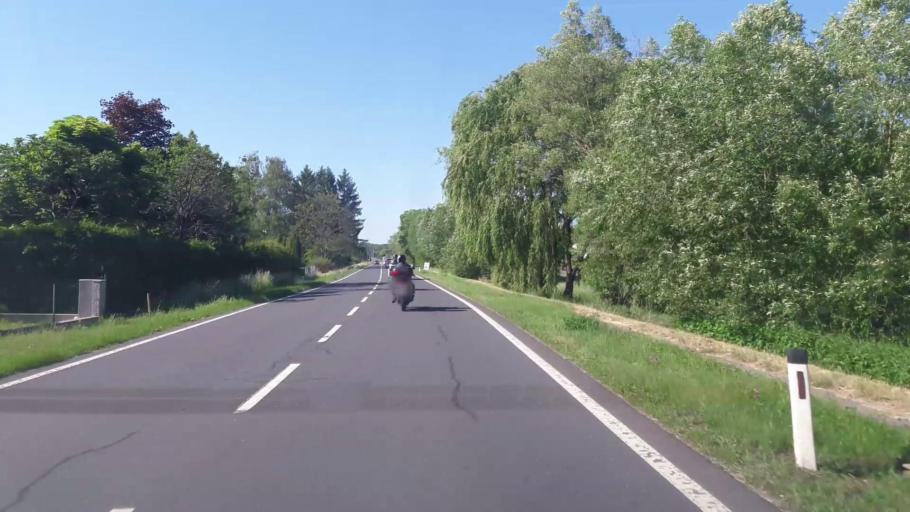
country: AT
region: Burgenland
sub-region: Politischer Bezirk Oberwart
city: Kemeten
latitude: 47.2512
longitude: 16.1535
